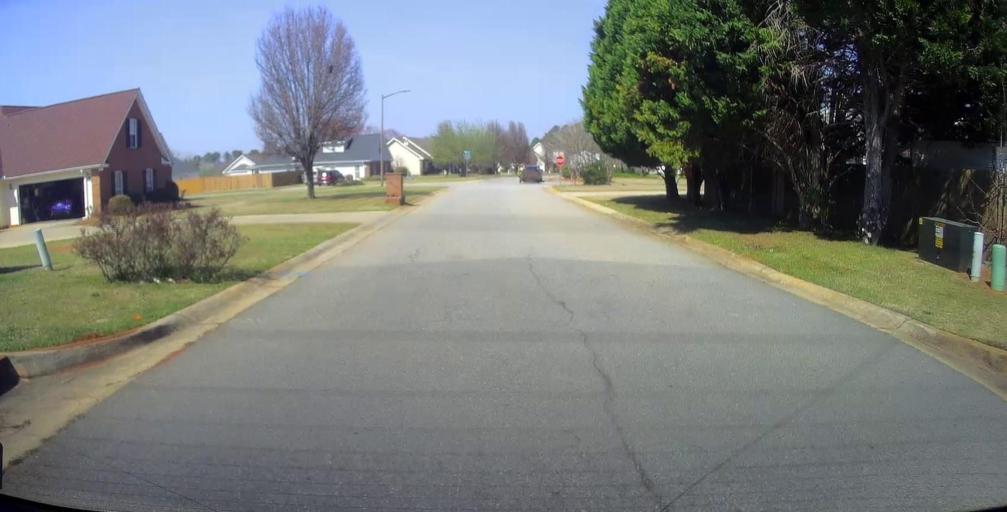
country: US
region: Georgia
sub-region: Houston County
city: Centerville
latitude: 32.5810
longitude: -83.7110
